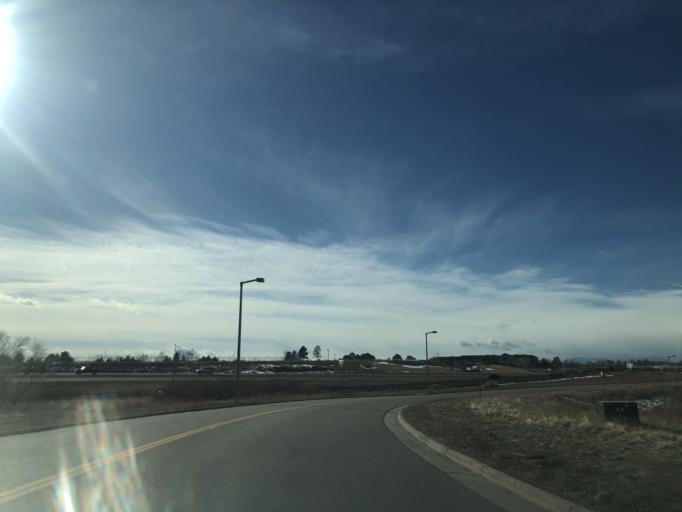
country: US
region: Colorado
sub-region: Douglas County
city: Meridian
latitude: 39.5520
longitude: -104.8468
